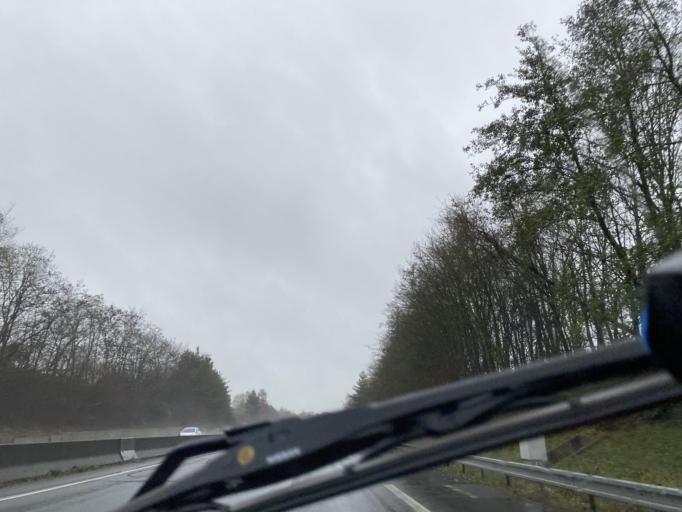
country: FR
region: Centre
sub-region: Departement du Cher
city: Vierzon
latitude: 47.2328
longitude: 2.0966
